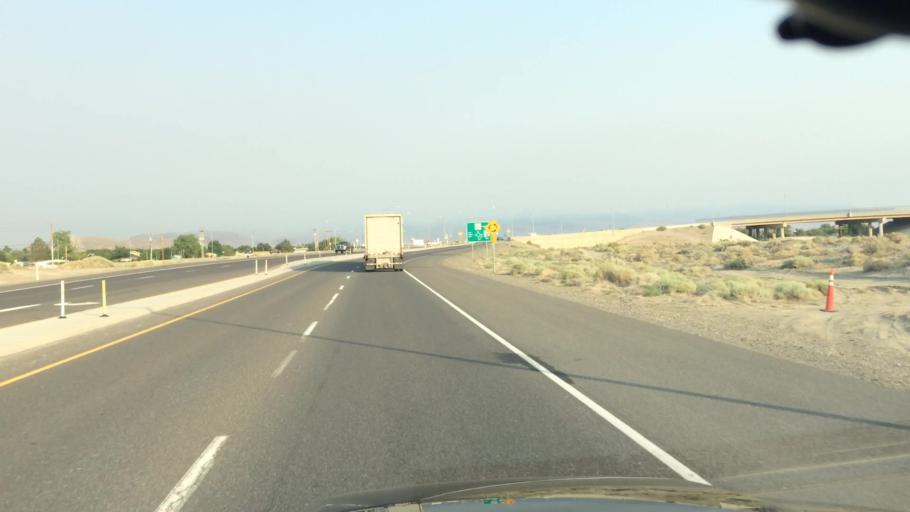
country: US
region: Nevada
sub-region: Lyon County
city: Fernley
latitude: 39.6024
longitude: -119.2231
